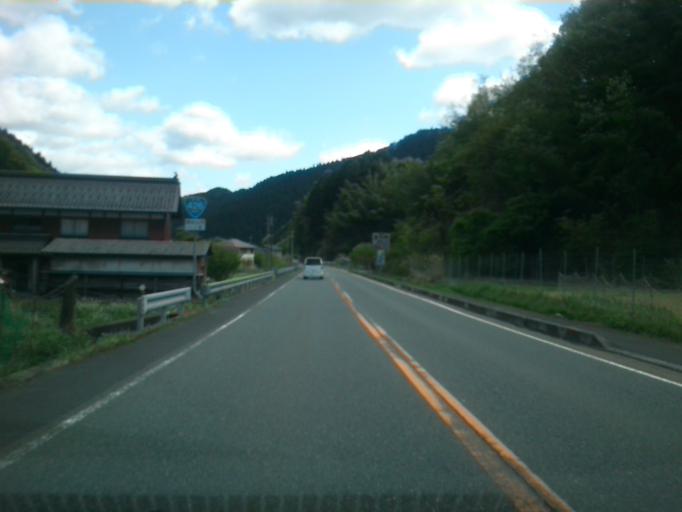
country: JP
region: Kyoto
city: Fukuchiyama
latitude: 35.3613
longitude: 135.0509
